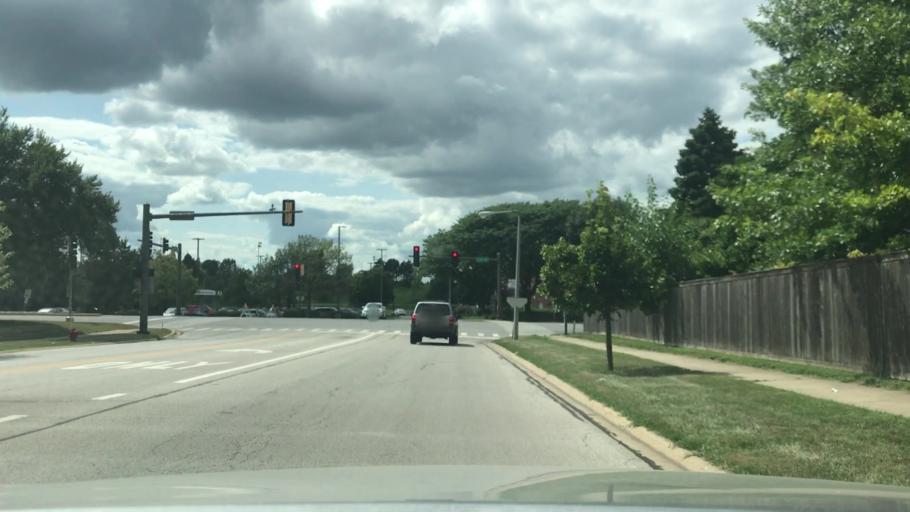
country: US
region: Illinois
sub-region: Kane County
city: Aurora
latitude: 41.7444
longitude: -88.2465
